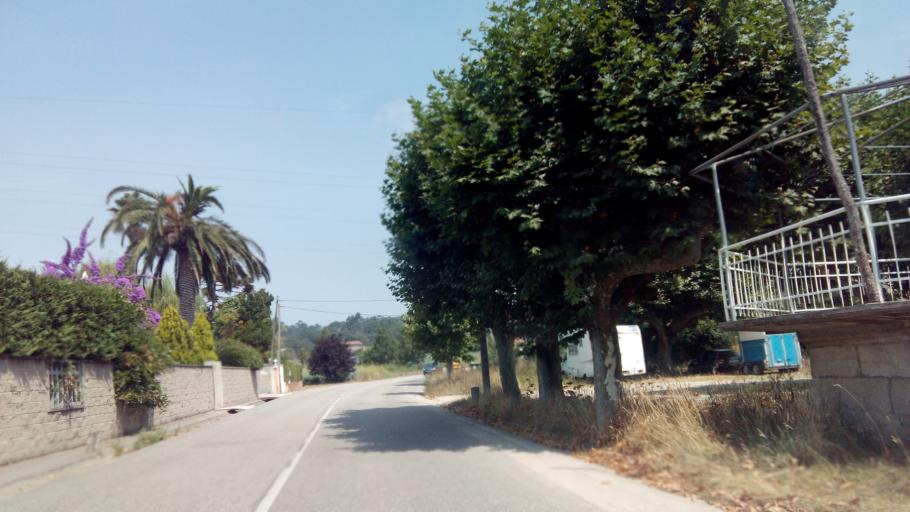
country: ES
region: Galicia
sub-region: Provincia de Pontevedra
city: Nigran
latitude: 42.1121
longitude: -8.8003
